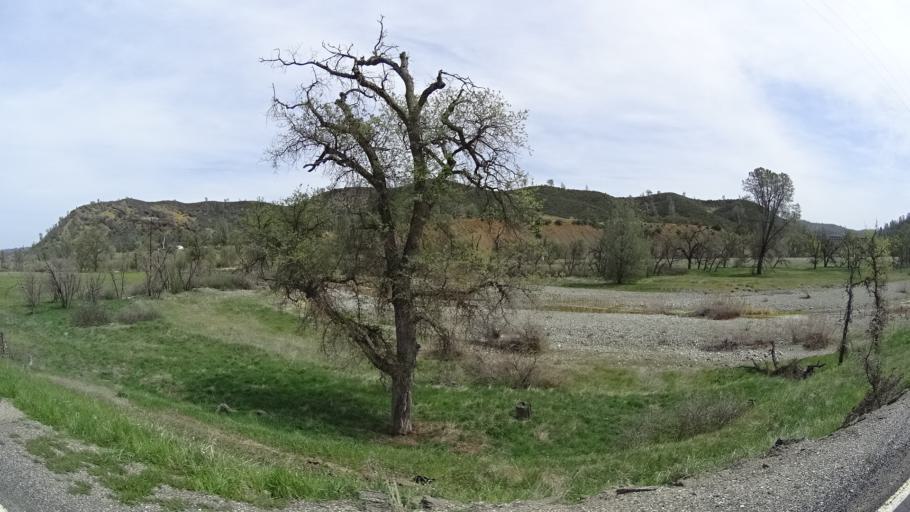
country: US
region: California
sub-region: Glenn County
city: Willows
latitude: 39.5918
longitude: -122.5411
